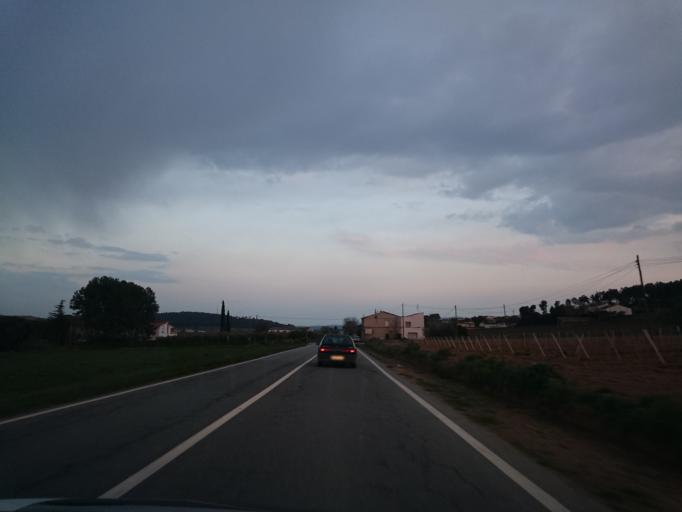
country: ES
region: Catalonia
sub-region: Provincia de Barcelona
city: Vilobi del Penedes
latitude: 41.3717
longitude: 1.6498
